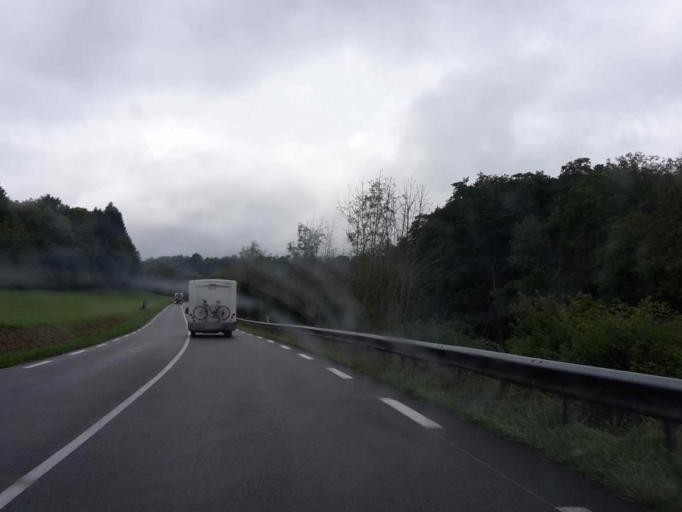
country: FR
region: Franche-Comte
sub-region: Departement du Doubs
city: Novillars
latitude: 47.3047
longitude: 6.1736
